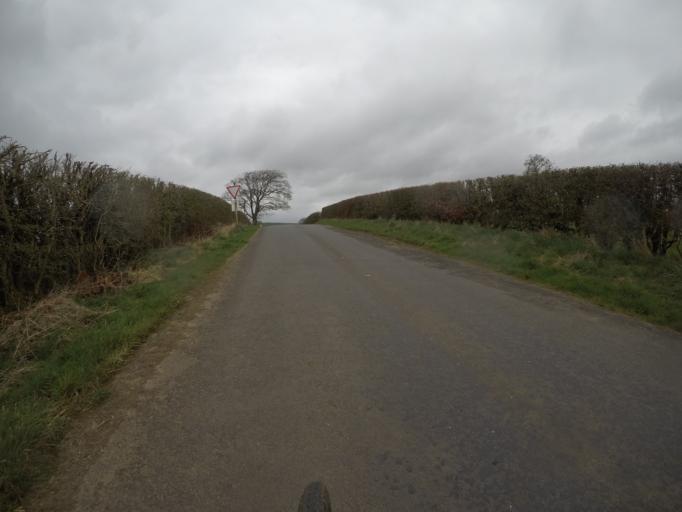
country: GB
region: Scotland
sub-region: East Ayrshire
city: Galston
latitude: 55.6194
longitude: -4.4352
